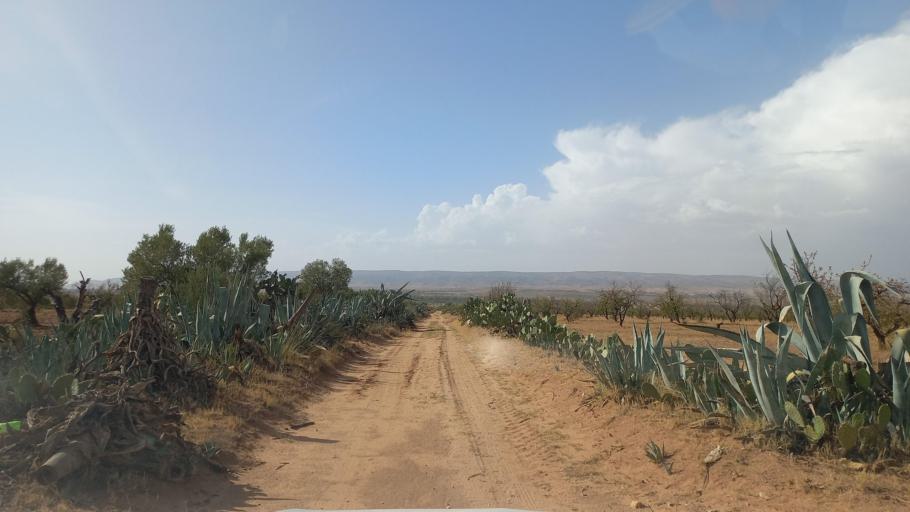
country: TN
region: Al Qasrayn
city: Kasserine
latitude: 35.2069
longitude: 8.9587
